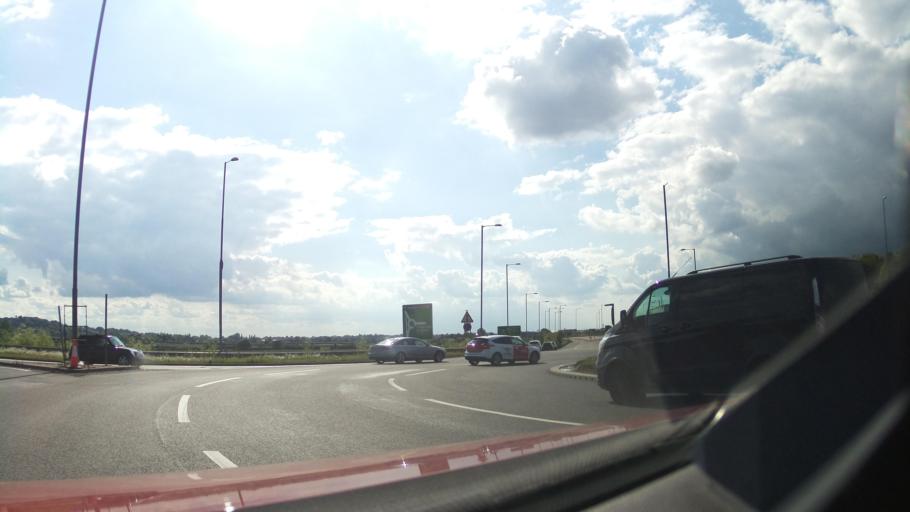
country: GB
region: England
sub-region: Central Bedfordshire
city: Husborne Crawley
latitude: 52.0252
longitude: -0.6029
